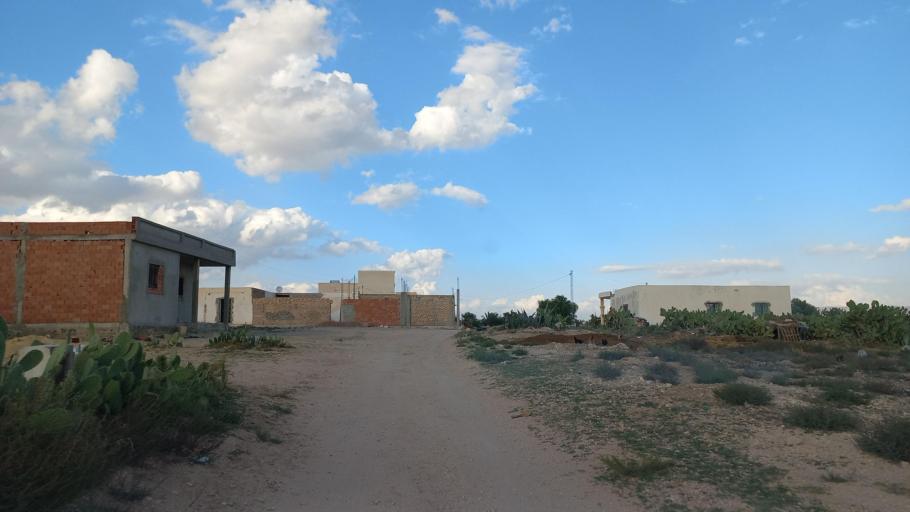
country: TN
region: Al Qasrayn
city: Sbiba
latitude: 35.3846
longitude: 9.0458
